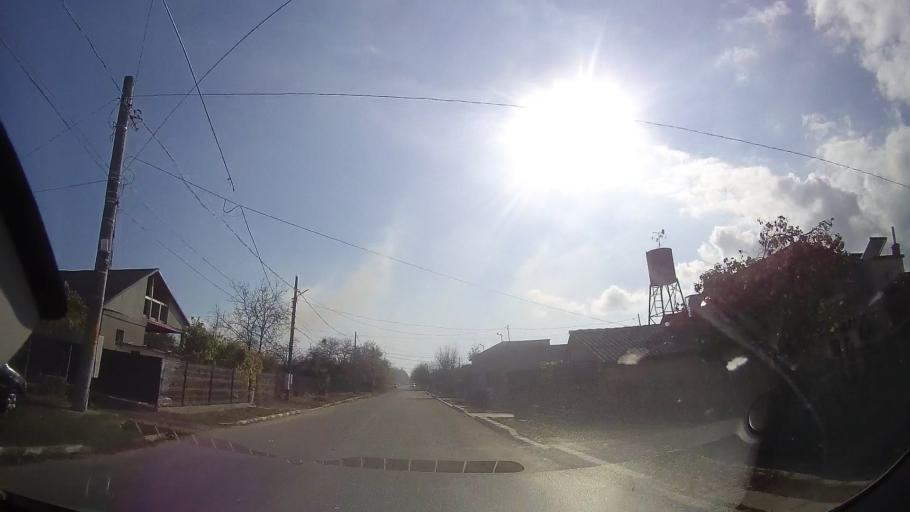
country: RO
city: Eforie Sud
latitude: 44.0122
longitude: 28.6439
